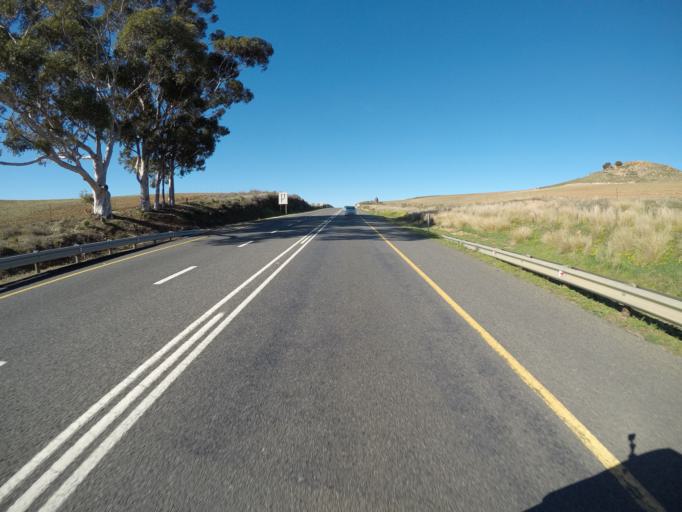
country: ZA
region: Western Cape
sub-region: Overberg District Municipality
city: Caledon
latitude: -34.2323
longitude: 19.2425
